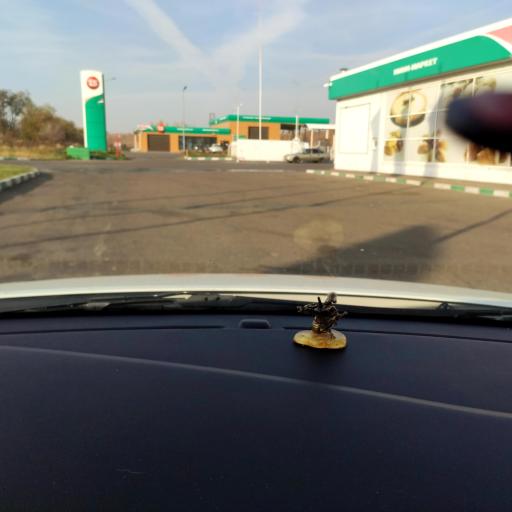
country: RU
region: Tatarstan
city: Osinovo
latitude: 55.9020
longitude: 48.9293
